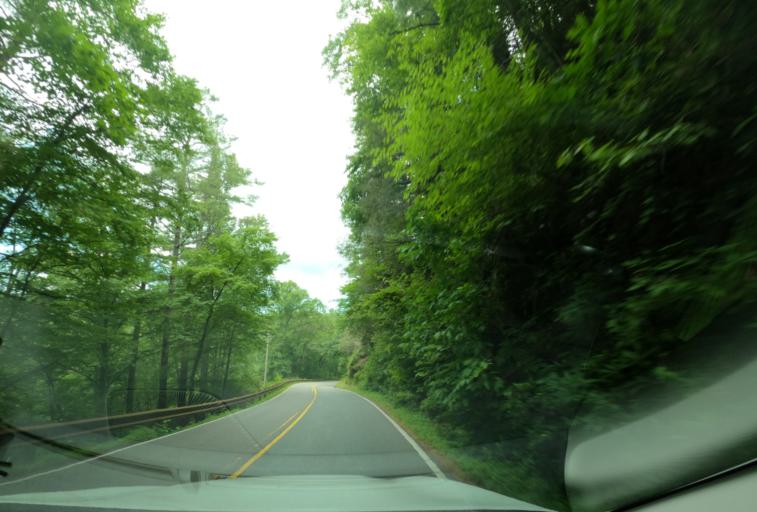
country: US
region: North Carolina
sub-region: Macon County
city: Franklin
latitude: 35.0704
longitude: -83.2289
